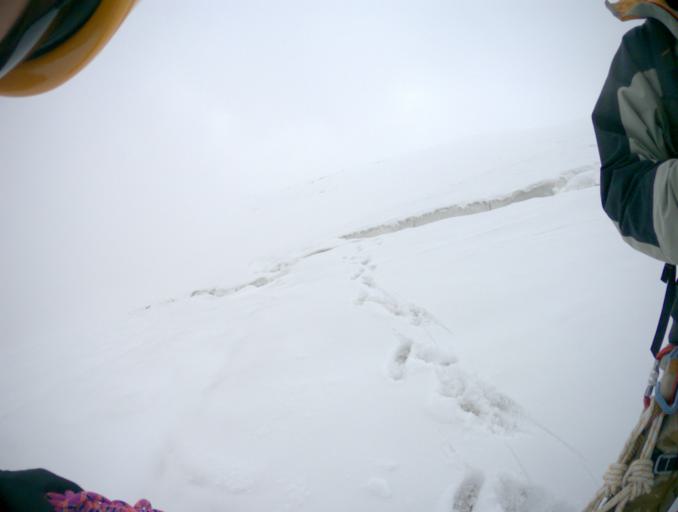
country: RU
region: Kabardino-Balkariya
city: Terskol
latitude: 43.3756
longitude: 42.4785
